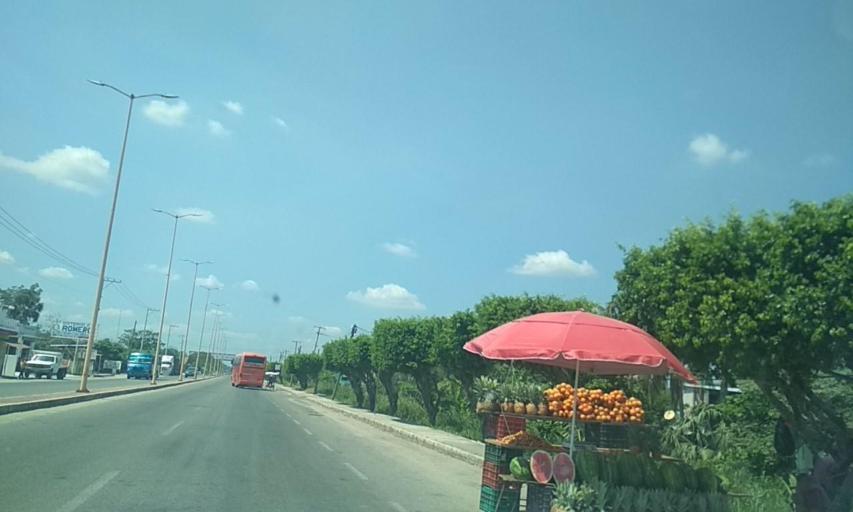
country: MX
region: Tabasco
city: Huimanguillo
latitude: 17.8389
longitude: -93.3977
